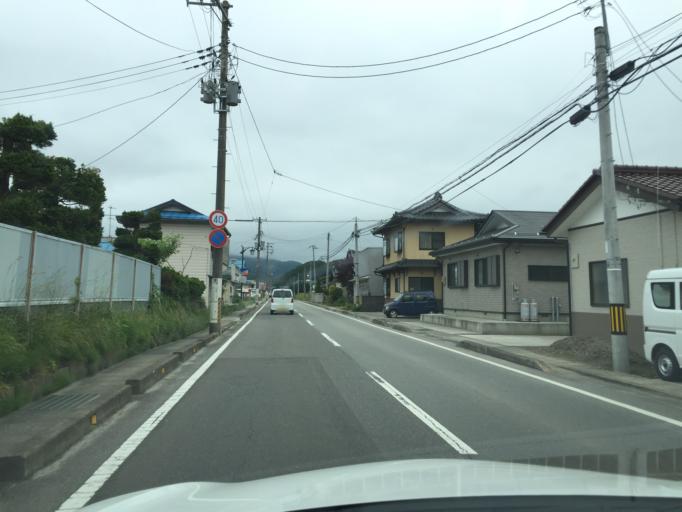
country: JP
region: Fukushima
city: Funehikimachi-funehiki
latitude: 37.3538
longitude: 140.6421
